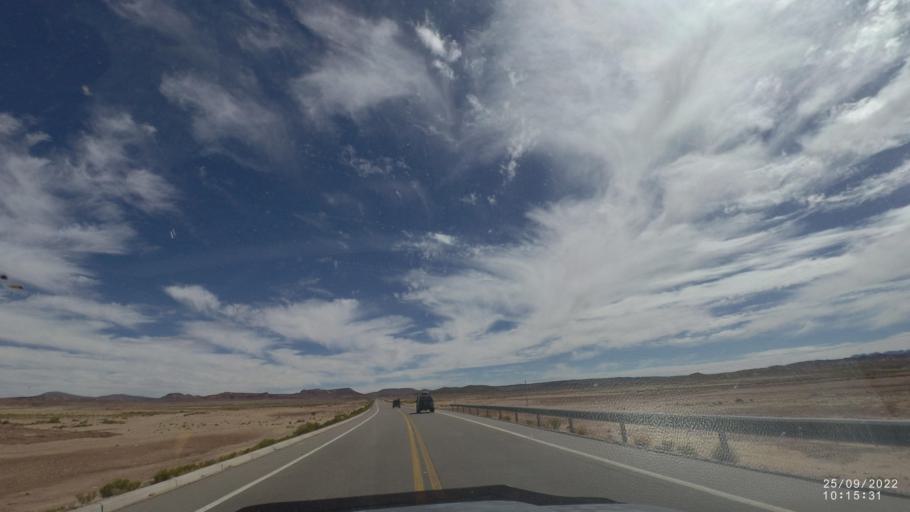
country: BO
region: Potosi
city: Colchani
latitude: -20.0466
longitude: -66.8695
